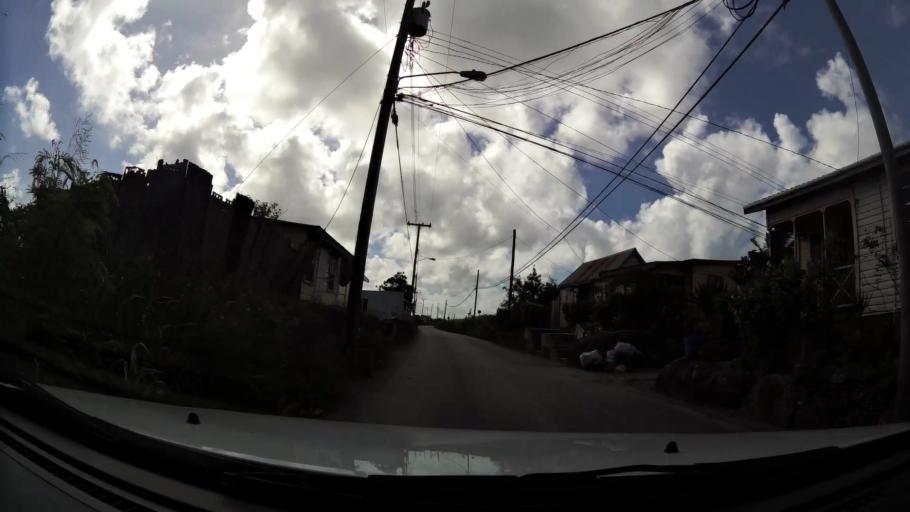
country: BB
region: Saint Lucy
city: Checker Hall
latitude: 13.2938
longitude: -59.6417
